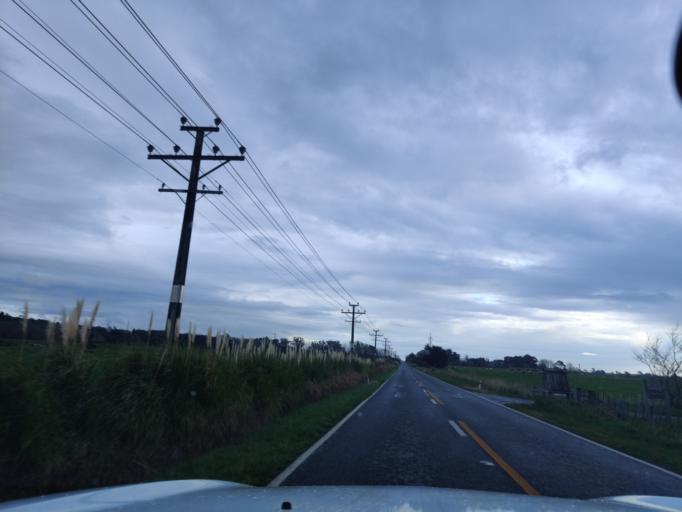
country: NZ
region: Manawatu-Wanganui
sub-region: Palmerston North City
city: Palmerston North
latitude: -40.3401
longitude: 175.7191
